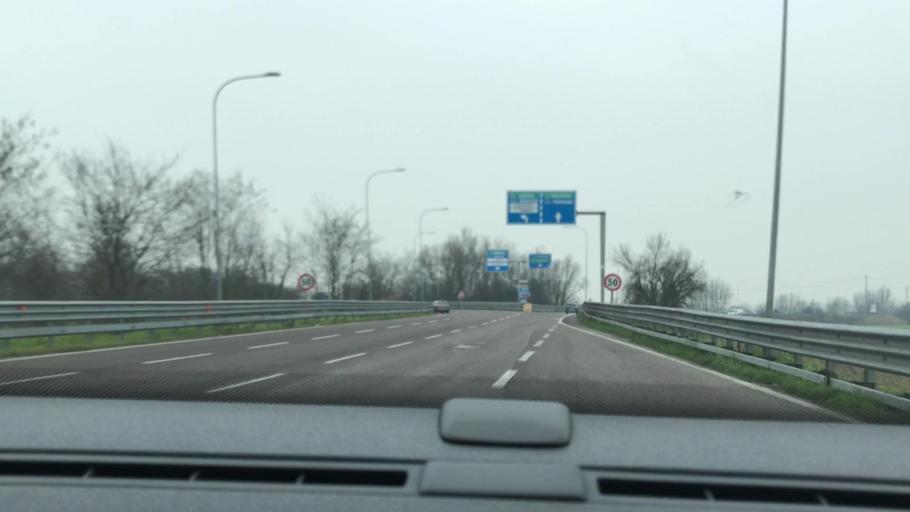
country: IT
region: Veneto
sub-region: Provincia di Rovigo
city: Bosaro
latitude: 45.0252
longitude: 11.7724
